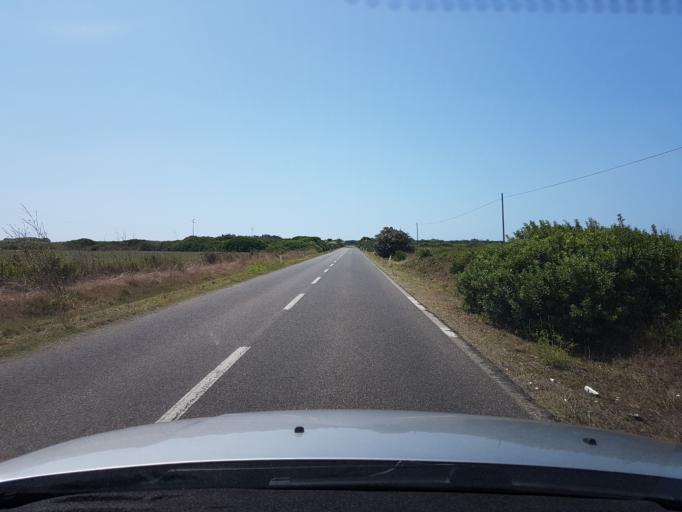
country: IT
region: Sardinia
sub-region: Provincia di Oristano
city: Riola Sardo
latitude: 40.0223
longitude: 8.4687
